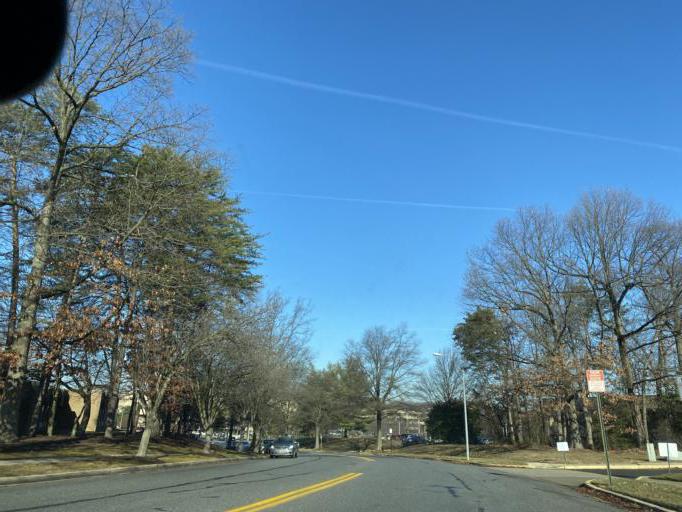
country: US
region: Maryland
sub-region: Prince George's County
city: West Laurel
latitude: 39.0846
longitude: -76.8787
